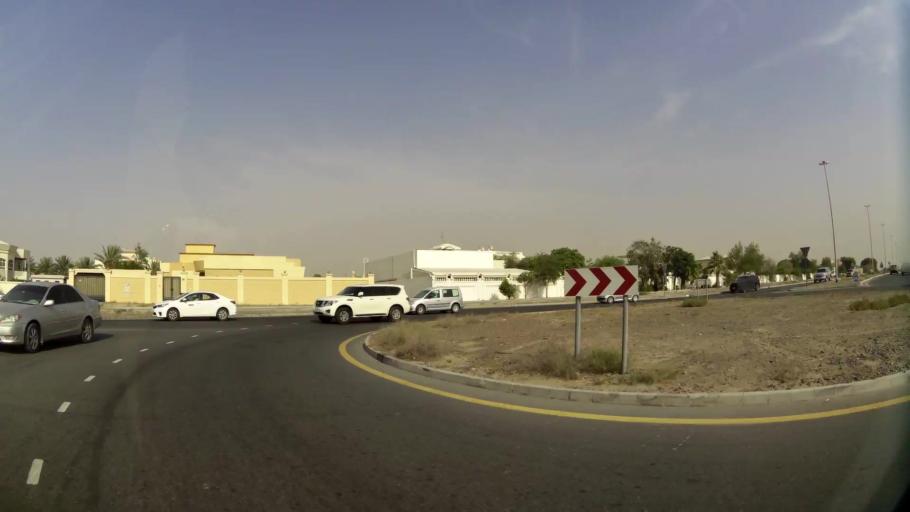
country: AE
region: Ash Shariqah
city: Sharjah
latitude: 25.2423
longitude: 55.4530
